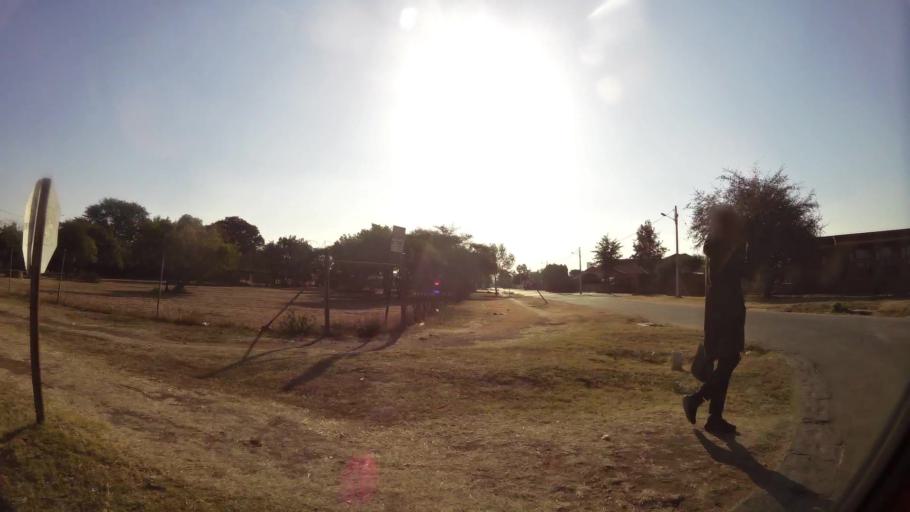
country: ZA
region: North-West
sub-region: Bojanala Platinum District Municipality
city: Rustenburg
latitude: -25.6453
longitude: 27.2428
